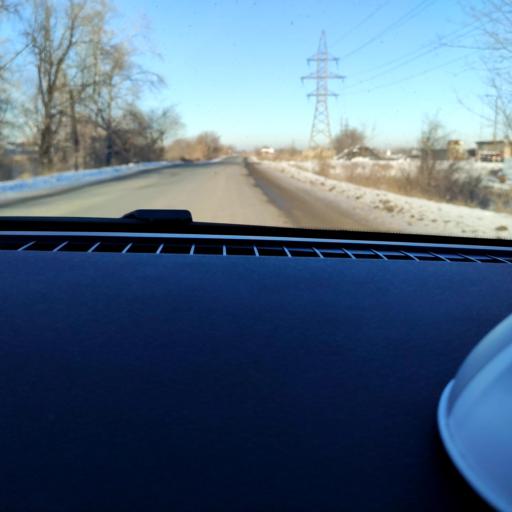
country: RU
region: Samara
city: Spiridonovka
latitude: 53.1084
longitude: 50.6403
